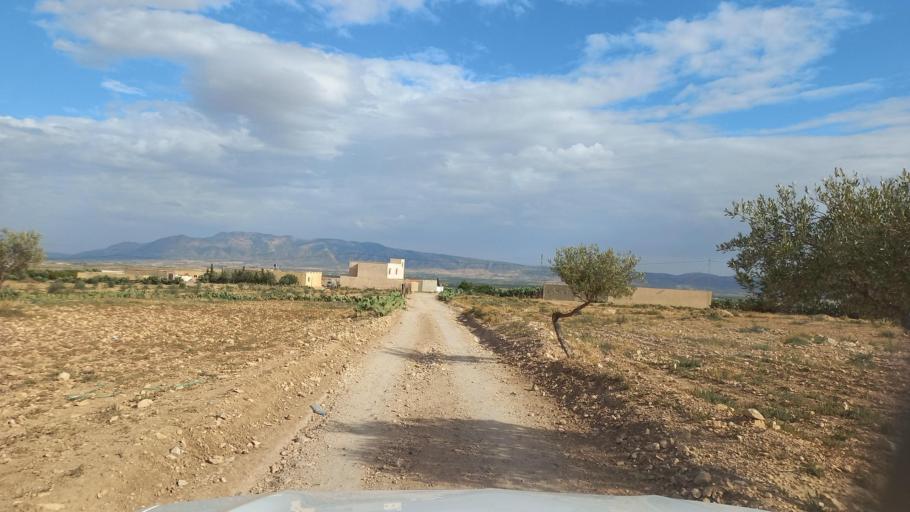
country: TN
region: Al Qasrayn
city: Sbiba
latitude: 35.4502
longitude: 9.0830
